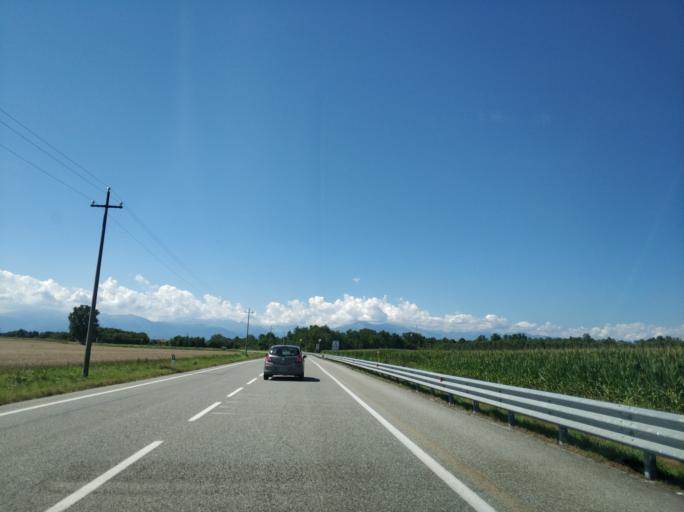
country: IT
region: Piedmont
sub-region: Provincia di Torino
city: Brandizzo
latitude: 45.2044
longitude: 7.8317
